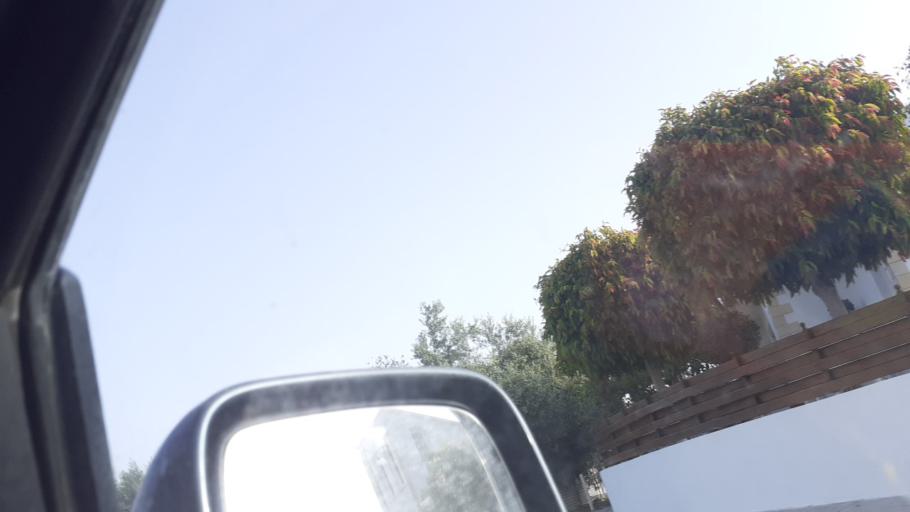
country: CY
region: Limassol
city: Ypsonas
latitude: 34.6577
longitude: 32.9659
